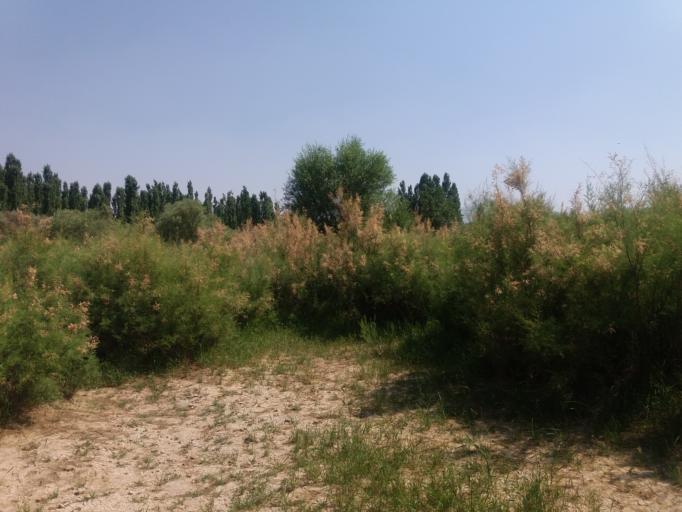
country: IR
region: Markazi
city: Shazand
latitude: 34.0824
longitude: 49.3523
